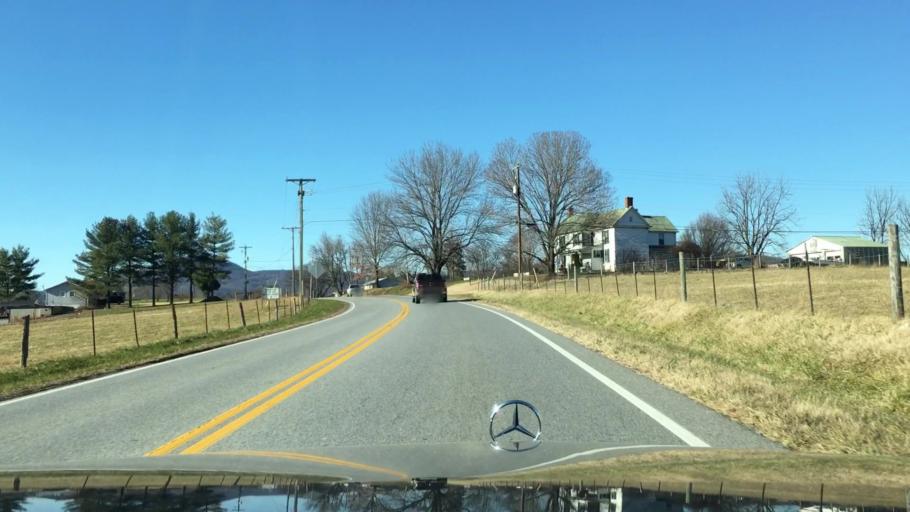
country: US
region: Virginia
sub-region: Botetourt County
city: Blue Ridge
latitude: 37.2671
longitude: -79.7590
